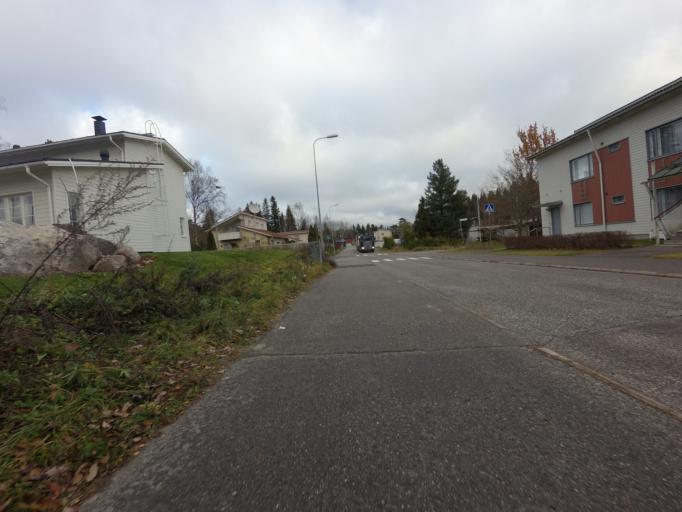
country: FI
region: Uusimaa
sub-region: Helsinki
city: Kauniainen
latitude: 60.1985
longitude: 24.7027
